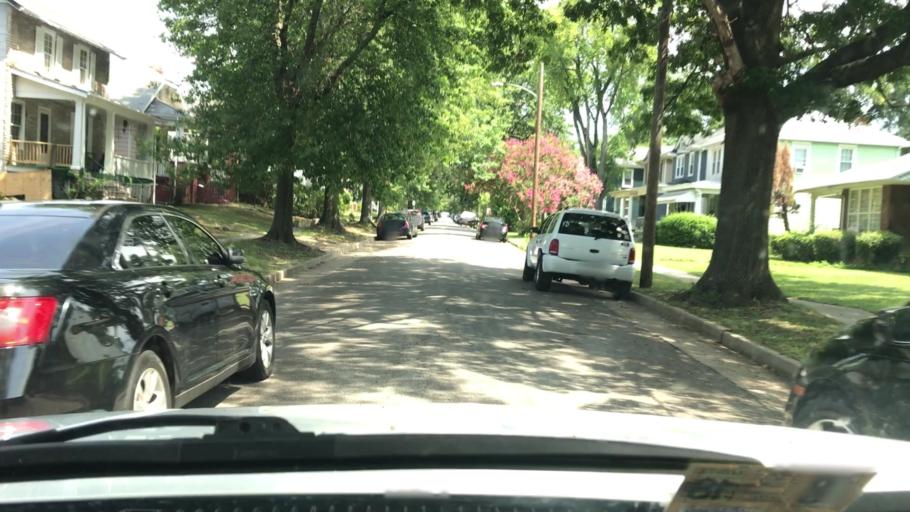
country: US
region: Virginia
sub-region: City of Richmond
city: Richmond
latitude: 37.5680
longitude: -77.4389
